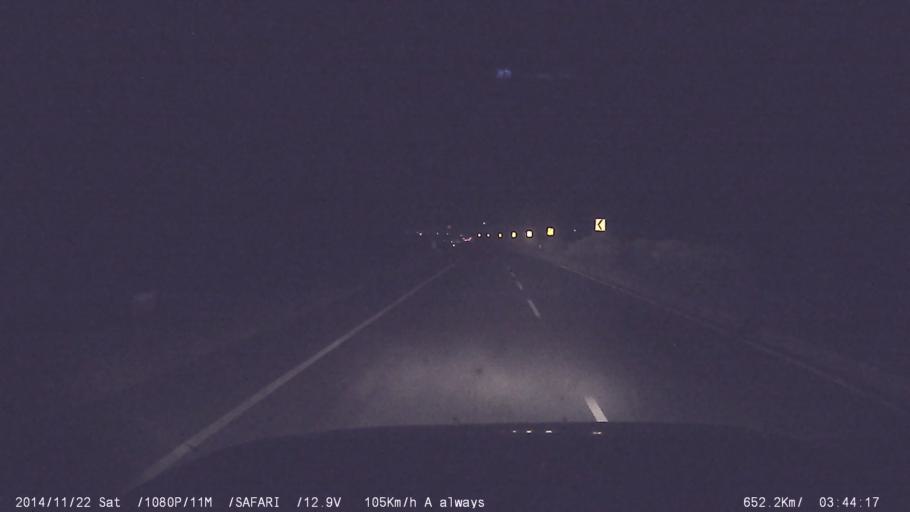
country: IN
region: Tamil Nadu
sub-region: Erode
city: Bhavani
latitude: 11.4506
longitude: 77.7649
